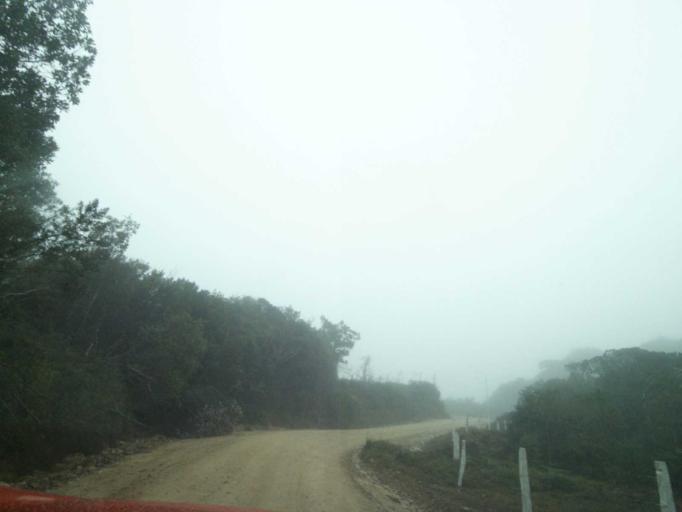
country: BR
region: Santa Catarina
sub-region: Anitapolis
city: Anitapolis
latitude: -27.9063
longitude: -49.1638
